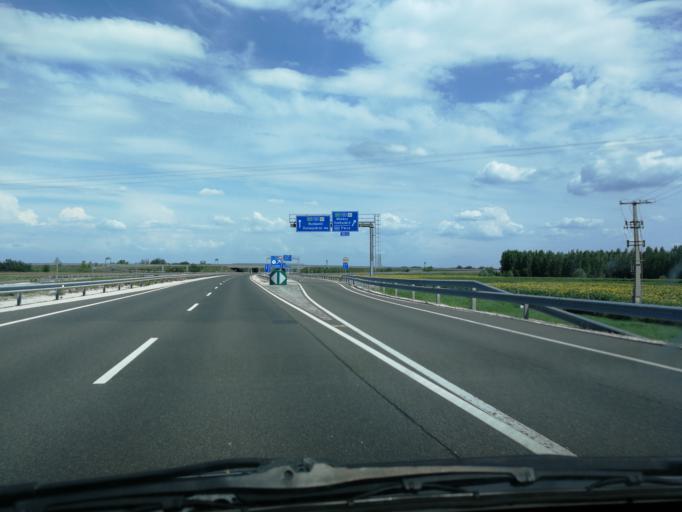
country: HU
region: Tolna
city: Szekszard
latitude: 46.3812
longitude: 18.7463
